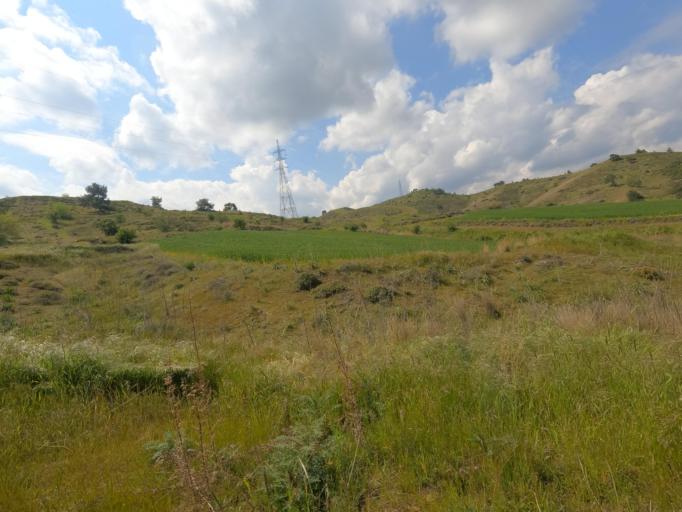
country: CY
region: Lefkosia
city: Kakopetria
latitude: 35.0768
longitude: 32.9428
